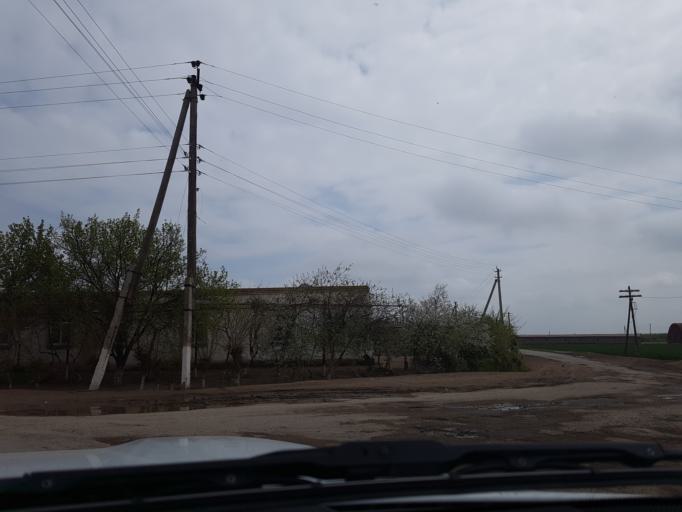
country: TM
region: Lebap
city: Turkmenabat
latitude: 38.9711
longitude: 63.6862
